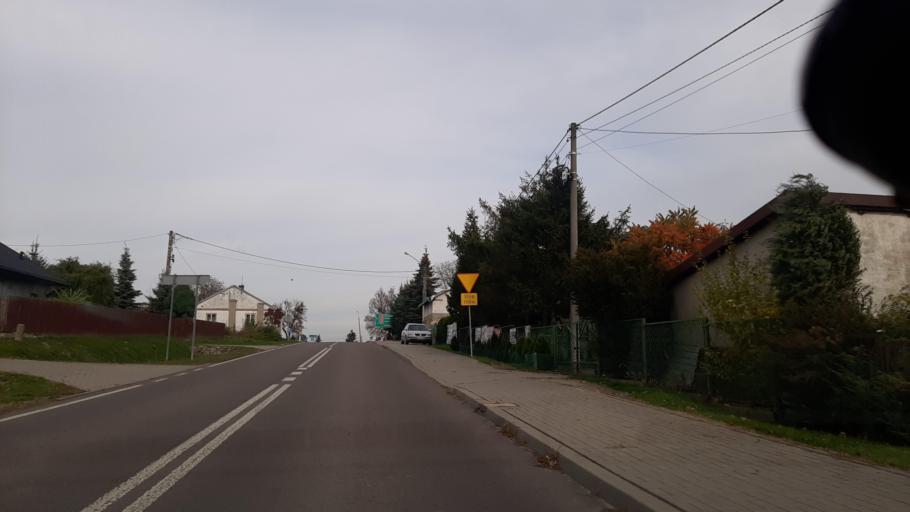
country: PL
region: Lublin Voivodeship
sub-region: Powiat pulawski
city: Markuszow
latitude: 51.3677
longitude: 22.2802
